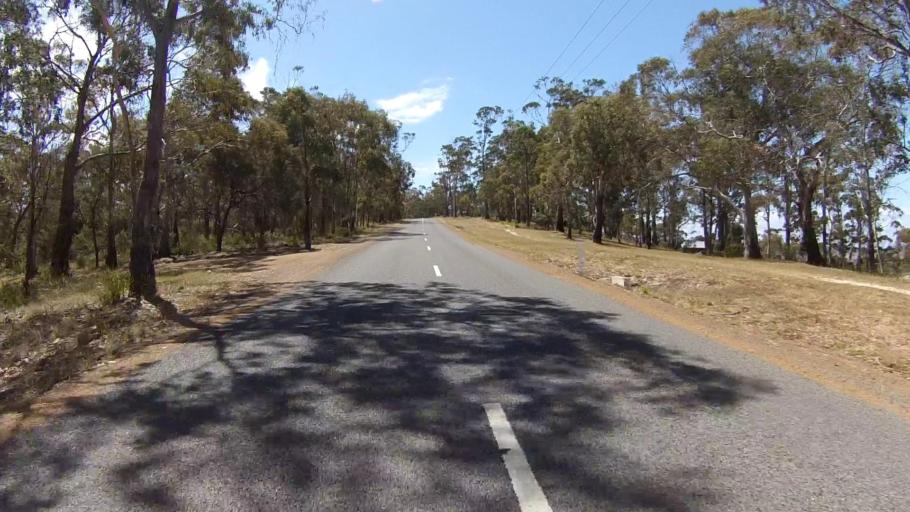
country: AU
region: Tasmania
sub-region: Clarence
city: Sandford
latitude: -43.0186
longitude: 147.4818
